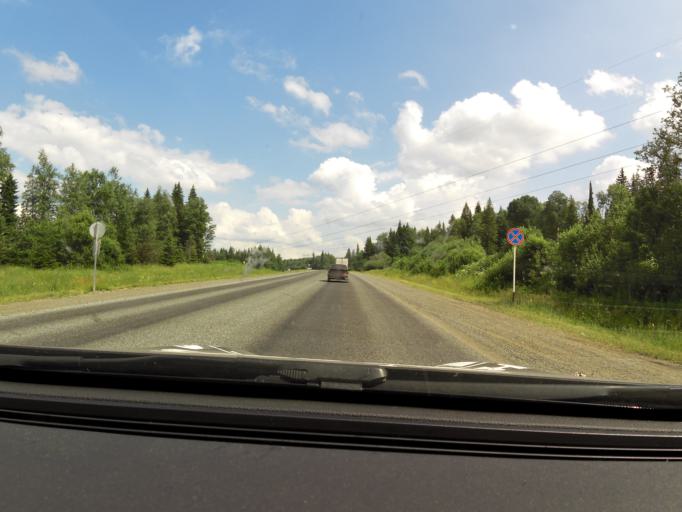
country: RU
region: Sverdlovsk
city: Arti
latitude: 56.7869
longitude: 58.5146
